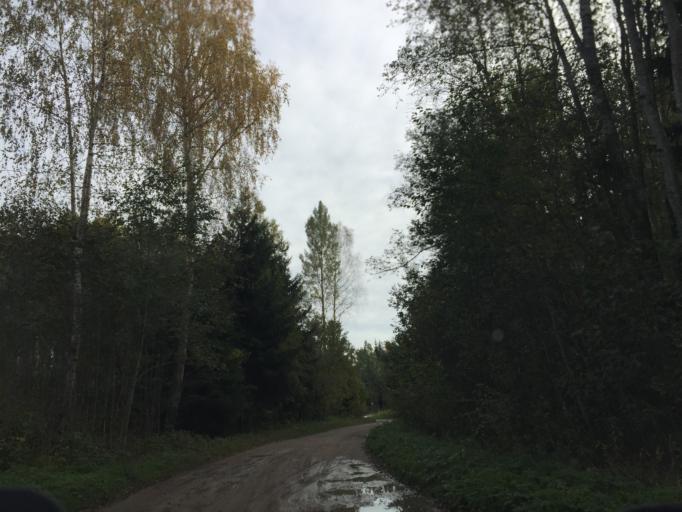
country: LV
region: Jaunpils
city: Jaunpils
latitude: 56.5699
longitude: 23.0287
